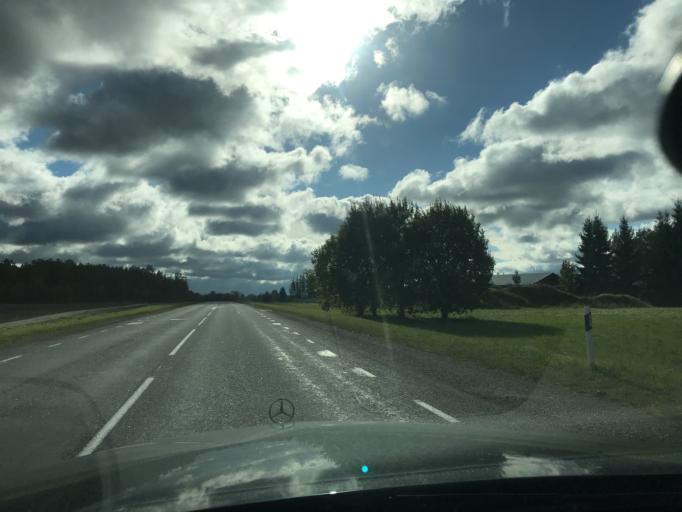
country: EE
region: Vorumaa
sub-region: Antsla vald
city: Vana-Antsla
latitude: 57.9354
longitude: 26.3138
